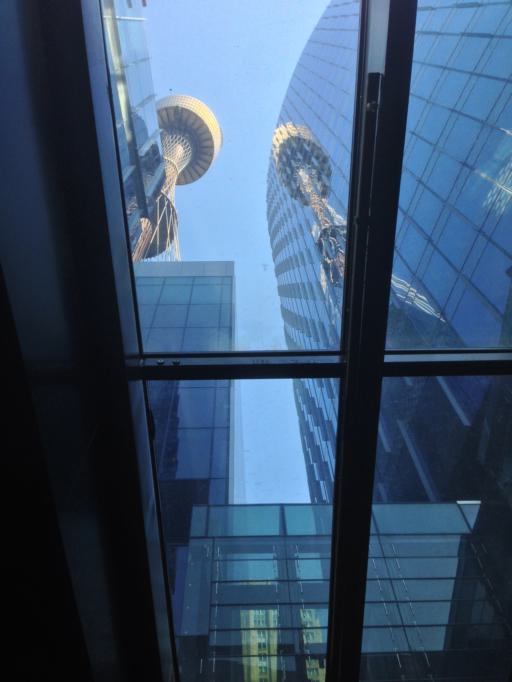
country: AU
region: New South Wales
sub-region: City of Sydney
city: Sydney
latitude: -33.8704
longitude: 151.2095
